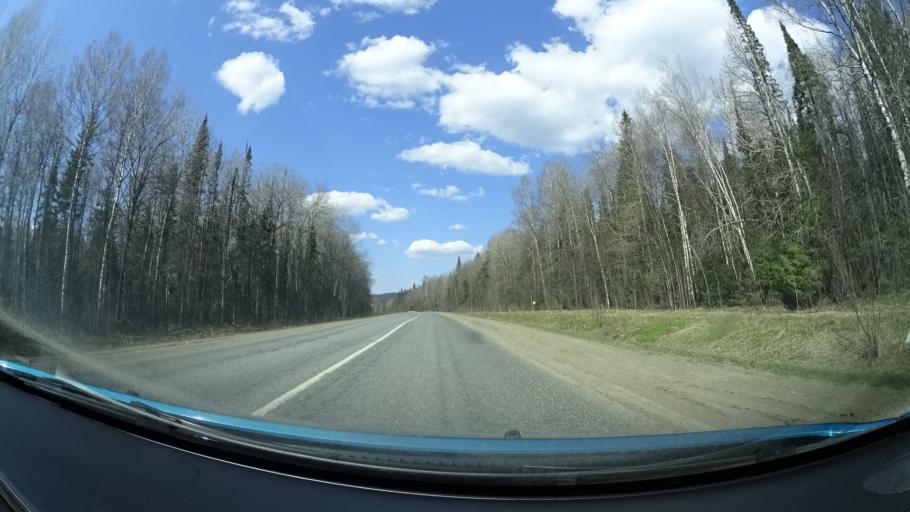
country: RU
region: Perm
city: Yugo-Kamskiy
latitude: 57.5824
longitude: 55.6767
